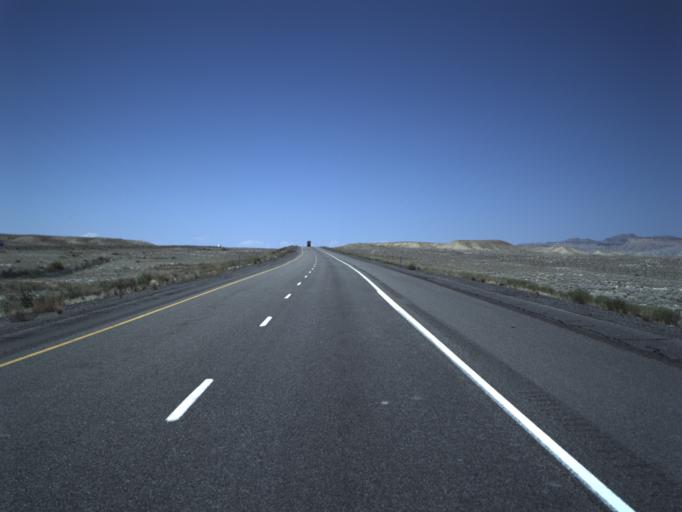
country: US
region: Utah
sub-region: Grand County
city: Moab
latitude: 38.9426
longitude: -109.5305
